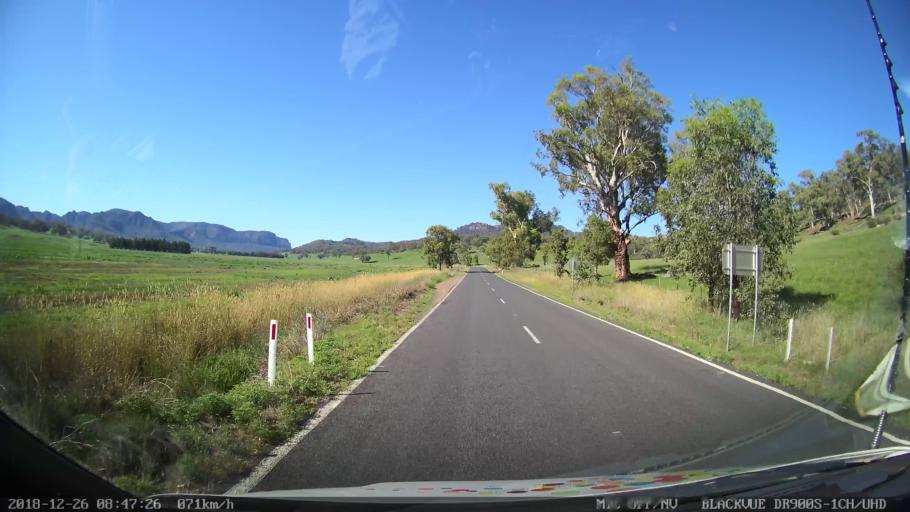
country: AU
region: New South Wales
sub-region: Mid-Western Regional
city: Kandos
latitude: -32.5426
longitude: 150.0914
